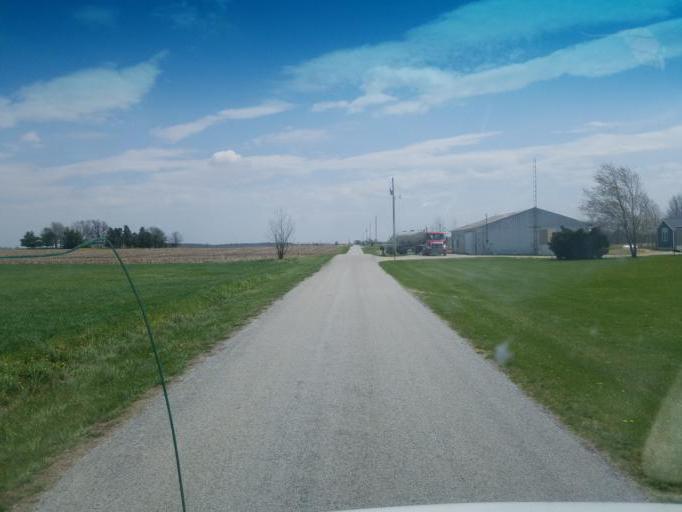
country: US
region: Ohio
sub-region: Hardin County
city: Forest
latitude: 40.7743
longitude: -83.4685
